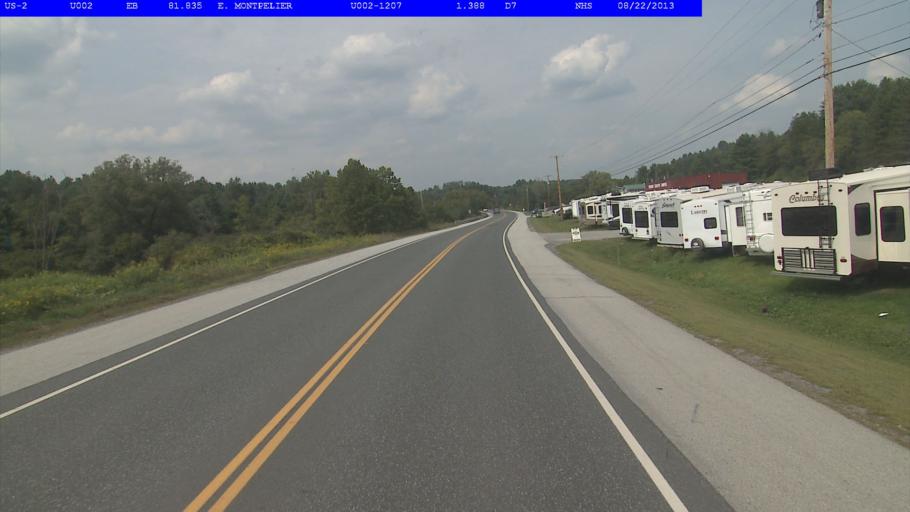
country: US
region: Vermont
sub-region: Washington County
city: Barre
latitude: 44.2531
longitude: -72.5021
